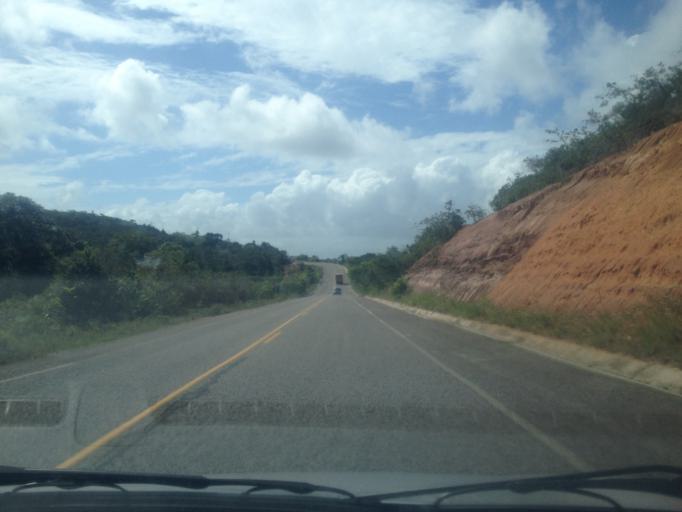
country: BR
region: Bahia
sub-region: Conde
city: Conde
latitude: -11.7203
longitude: -37.5750
